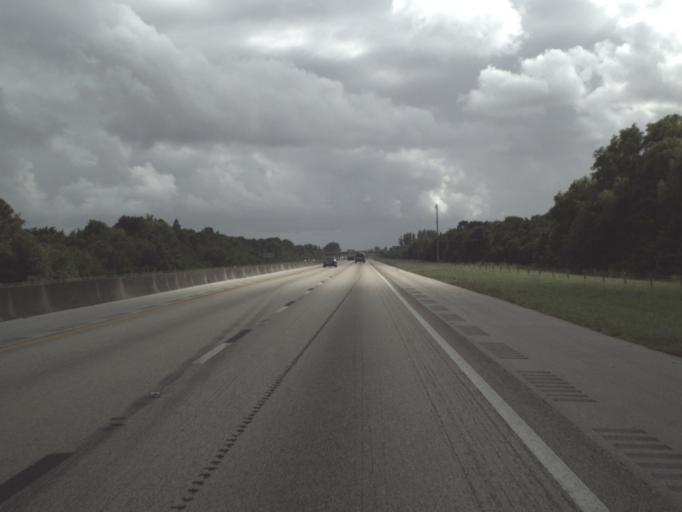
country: US
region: Florida
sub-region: Palm Beach County
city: Palm Beach Gardens
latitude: 26.8560
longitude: -80.1294
